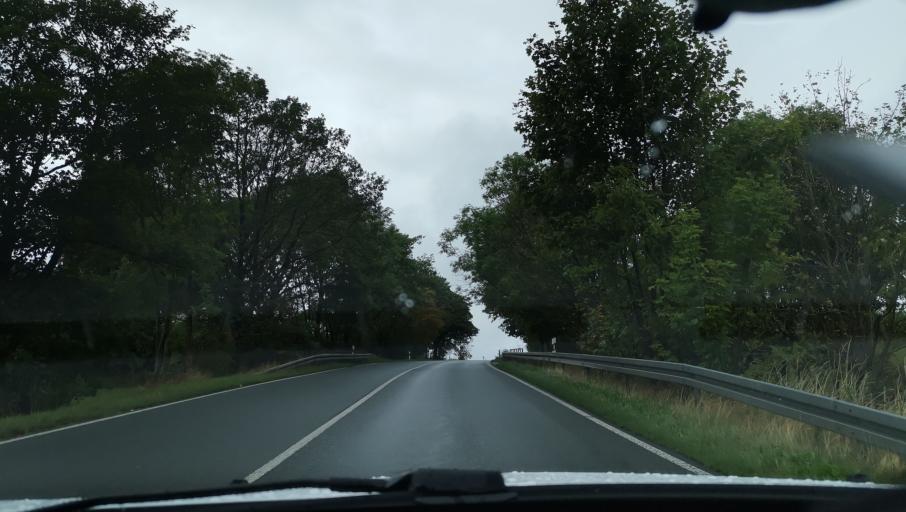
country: DE
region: North Rhine-Westphalia
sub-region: Regierungsbezirk Arnsberg
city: Breckerfeld
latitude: 51.2718
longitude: 7.4520
